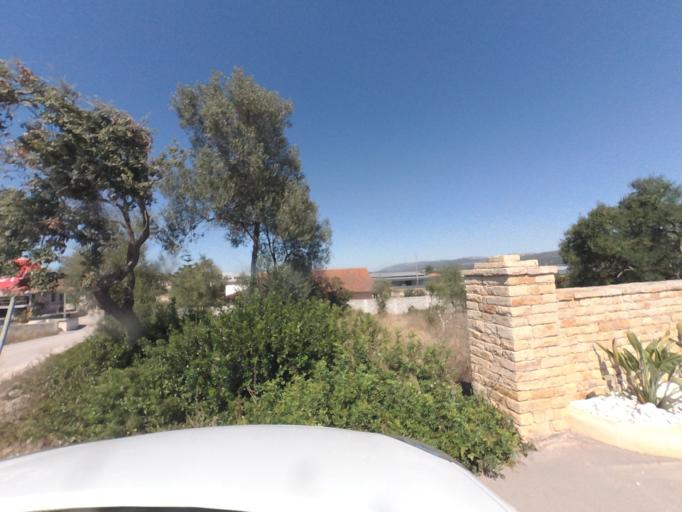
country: PT
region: Leiria
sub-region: Alcobaca
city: Turquel
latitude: 39.4626
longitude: -8.9716
